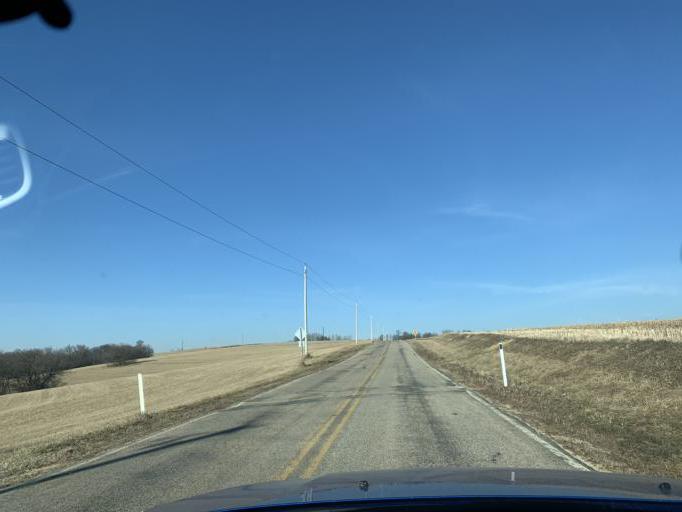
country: US
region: Wisconsin
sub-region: Iowa County
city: Barneveld
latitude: 42.8526
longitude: -89.9359
